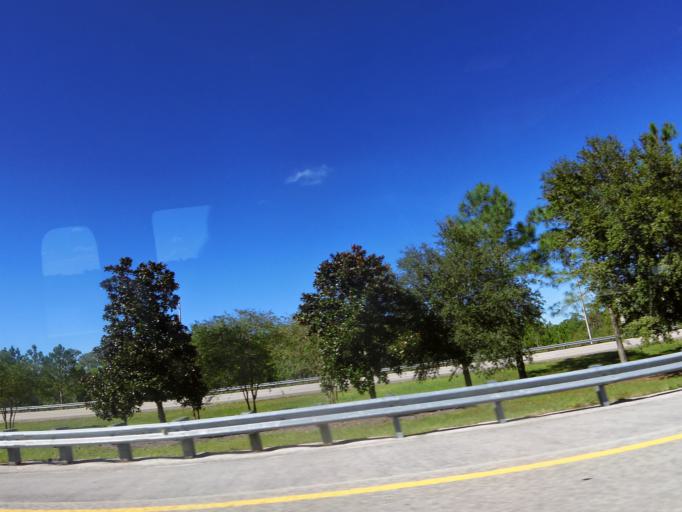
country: US
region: Florida
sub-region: Saint Johns County
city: Palm Valley
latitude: 30.1147
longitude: -81.4343
